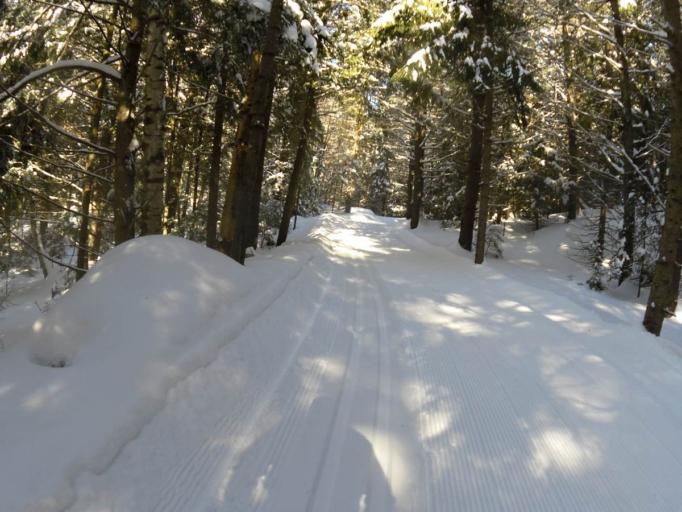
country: CA
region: Quebec
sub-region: Outaouais
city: Wakefield
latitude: 45.6227
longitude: -75.9469
